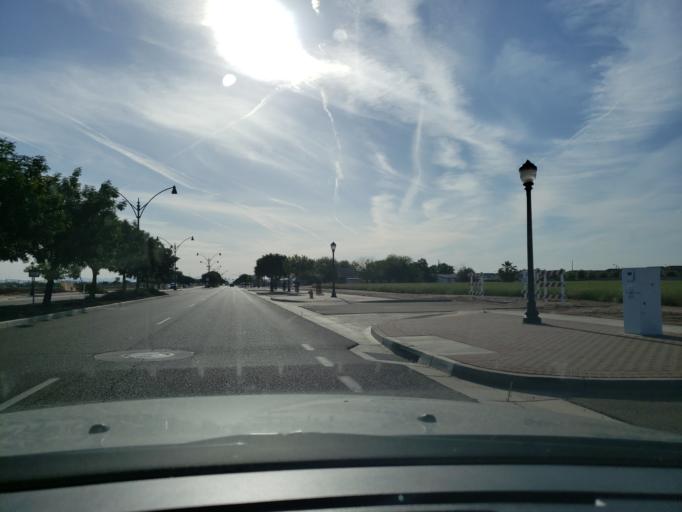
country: US
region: Arizona
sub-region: Maricopa County
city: Queen Creek
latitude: 33.3072
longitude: -111.6983
